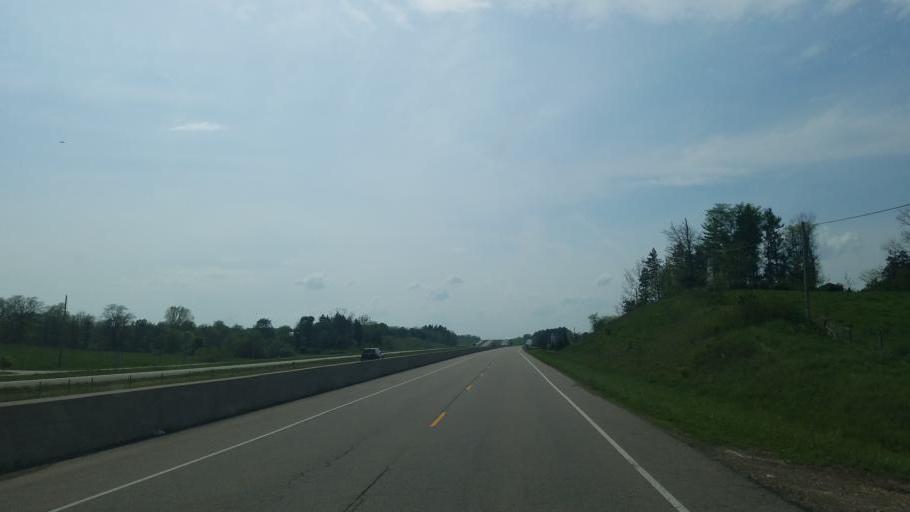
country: US
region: Ohio
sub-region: Licking County
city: Granville South
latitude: 40.0706
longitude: -82.5648
